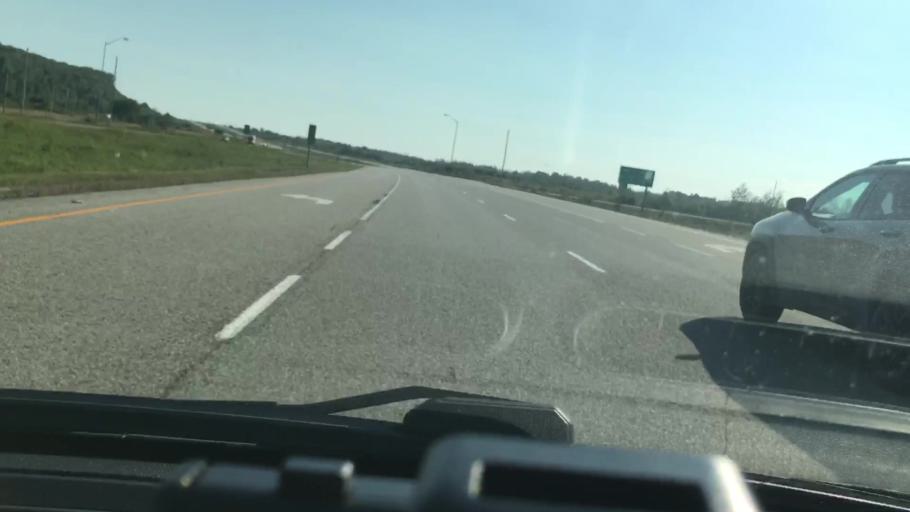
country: CA
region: Ontario
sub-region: Algoma
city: Sault Ste. Marie
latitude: 46.4721
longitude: -84.0579
